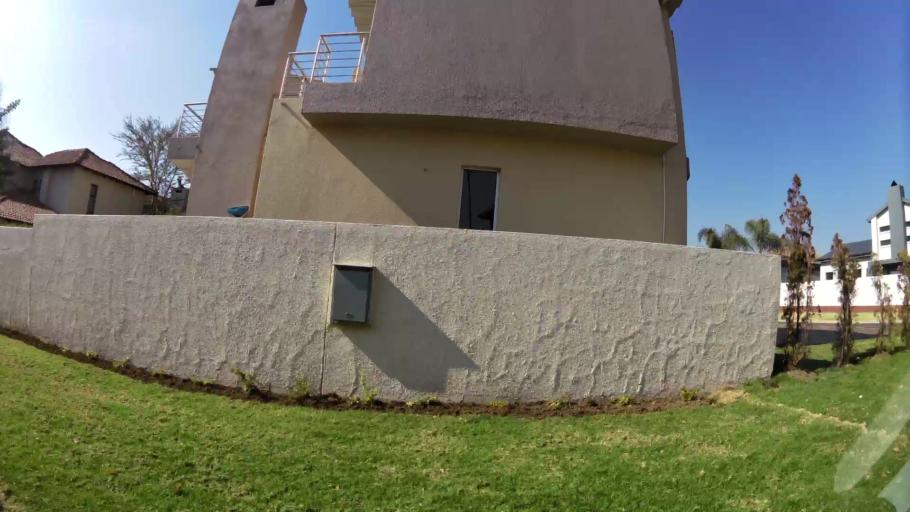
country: ZA
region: Gauteng
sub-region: City of Johannesburg Metropolitan Municipality
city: Modderfontein
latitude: -26.1178
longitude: 28.1529
